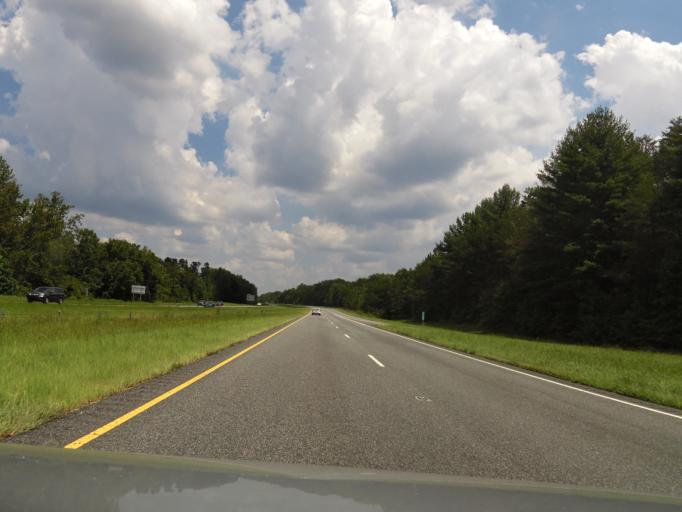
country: US
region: North Carolina
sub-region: Polk County
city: Columbus
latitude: 35.2825
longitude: -82.1118
